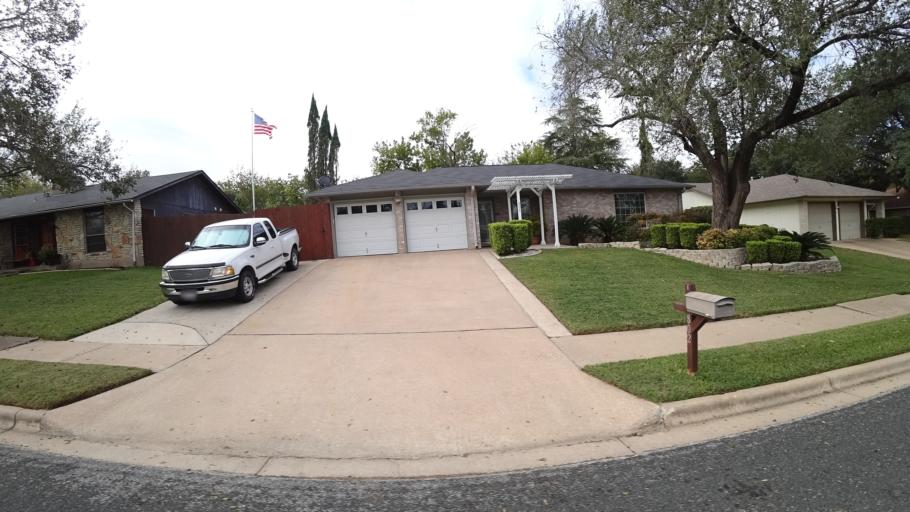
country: US
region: Texas
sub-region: Williamson County
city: Brushy Creek
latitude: 30.5164
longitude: -97.7363
